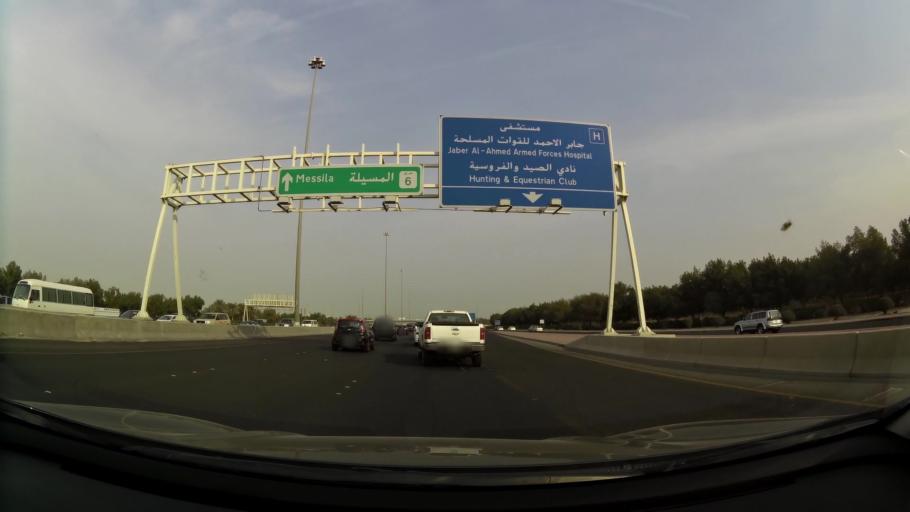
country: KW
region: Al Farwaniyah
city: Janub as Surrah
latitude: 29.2644
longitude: 48.0161
